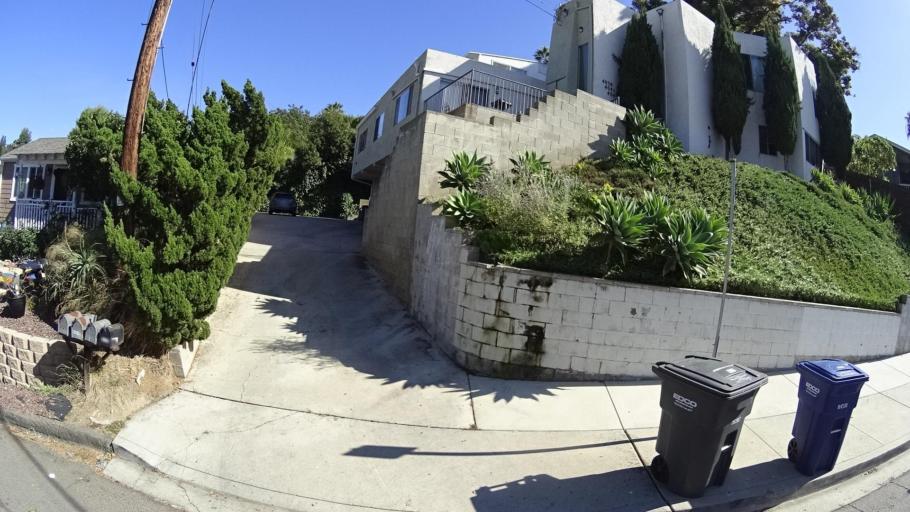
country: US
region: California
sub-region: San Diego County
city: Spring Valley
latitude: 32.7507
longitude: -116.9834
